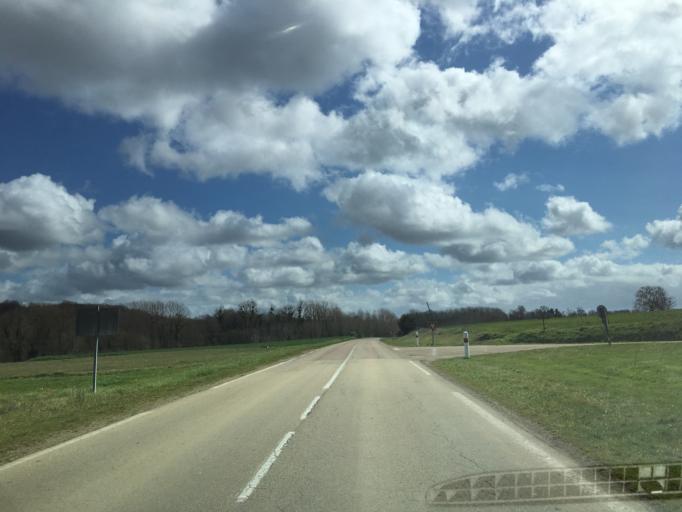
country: FR
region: Bourgogne
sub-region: Departement de l'Yonne
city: Fleury-la-Vallee
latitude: 47.8412
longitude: 3.3978
